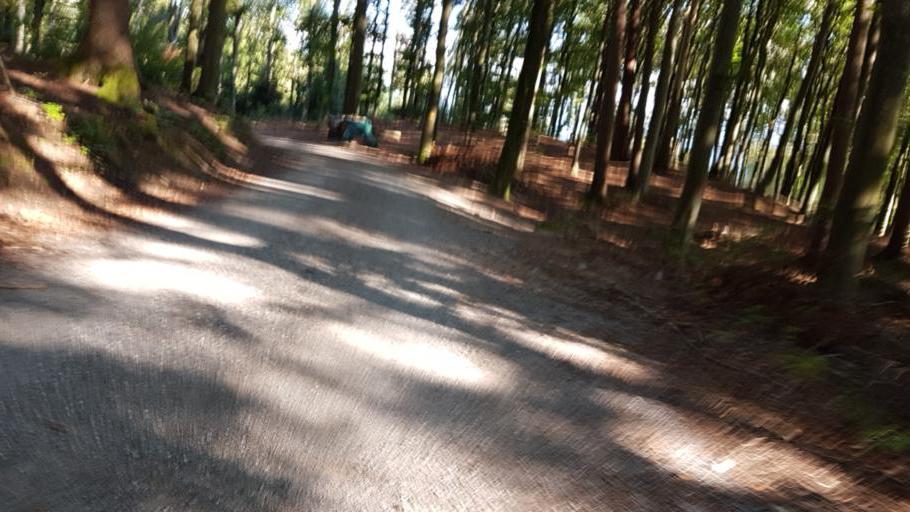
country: CH
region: Bern
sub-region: Bern-Mittelland District
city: Muri
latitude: 46.9431
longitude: 7.5045
